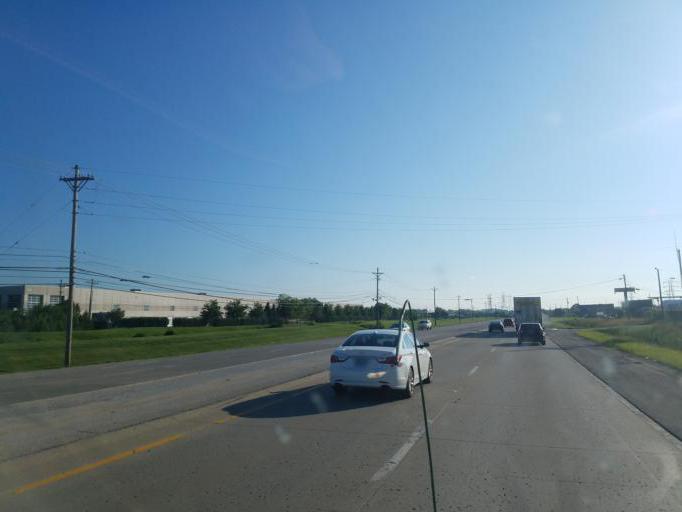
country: US
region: Kentucky
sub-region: Jefferson County
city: Heritage Creek
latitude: 38.1320
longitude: -85.7288
